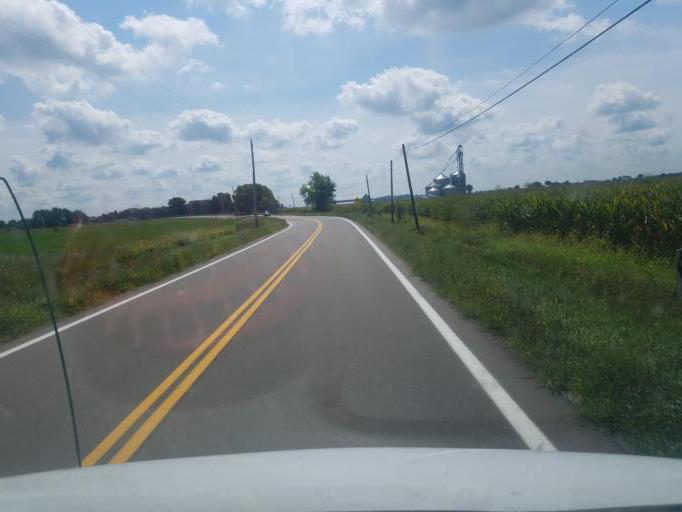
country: US
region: Ohio
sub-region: Marion County
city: Prospect
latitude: 40.3965
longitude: -83.1617
